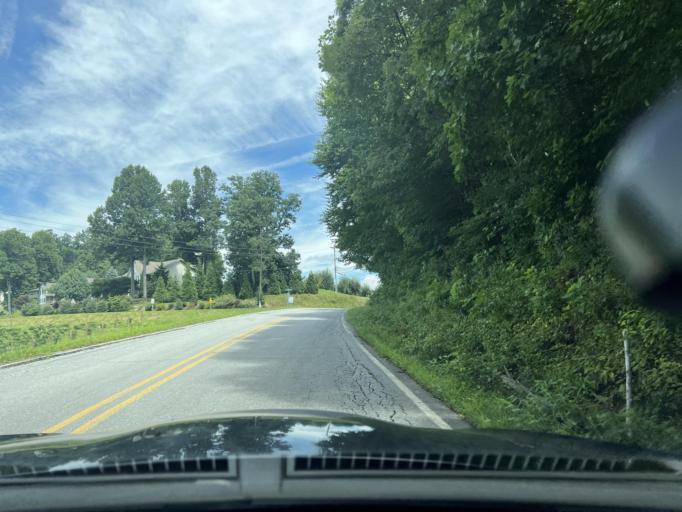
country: US
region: North Carolina
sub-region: Henderson County
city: Edneyville
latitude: 35.3828
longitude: -82.3132
